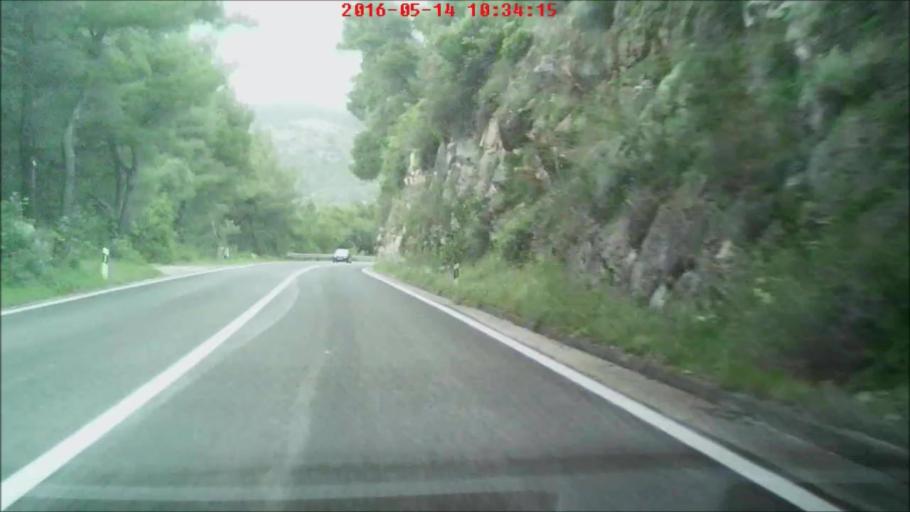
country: HR
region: Dubrovacko-Neretvanska
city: Podgora
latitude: 42.7798
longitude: 17.8905
